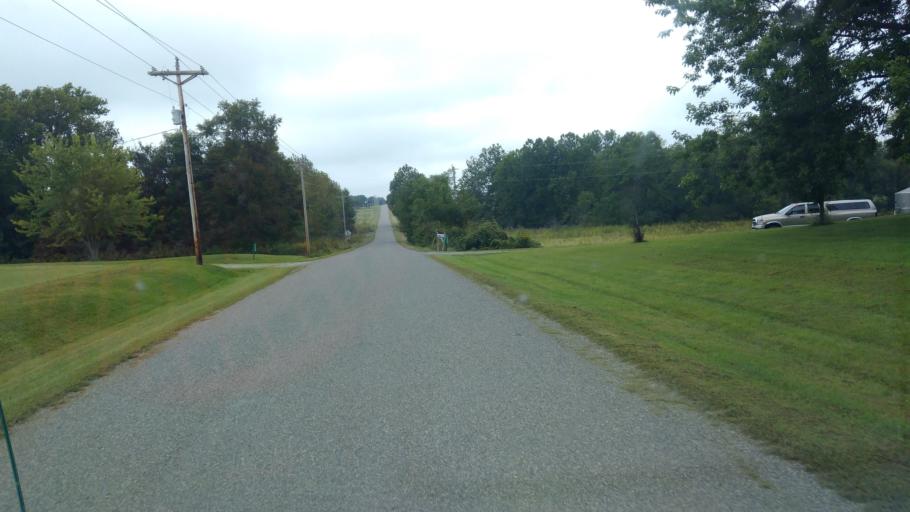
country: US
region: Ohio
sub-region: Hardin County
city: Kenton
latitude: 40.5779
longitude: -83.6650
